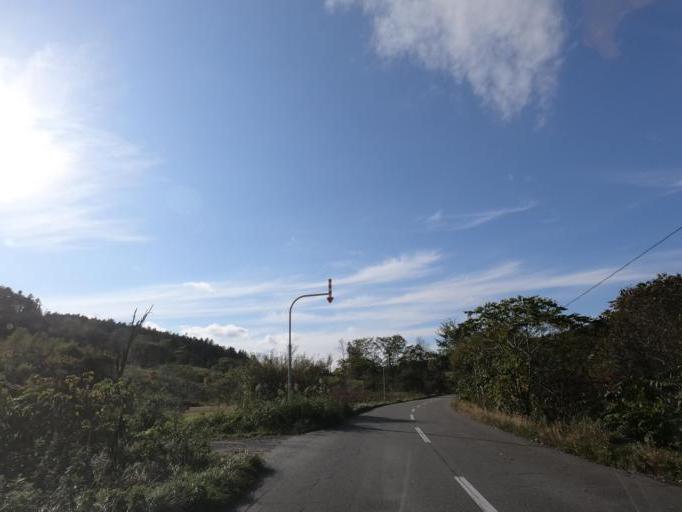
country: JP
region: Hokkaido
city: Obihiro
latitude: 42.6171
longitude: 143.4105
